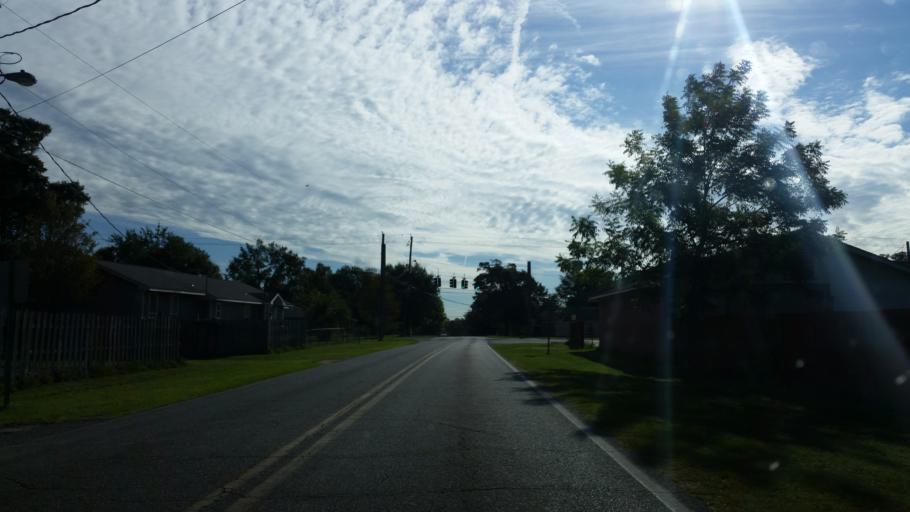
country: US
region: Florida
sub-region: Santa Rosa County
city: Milton
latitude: 30.6333
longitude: -87.0407
